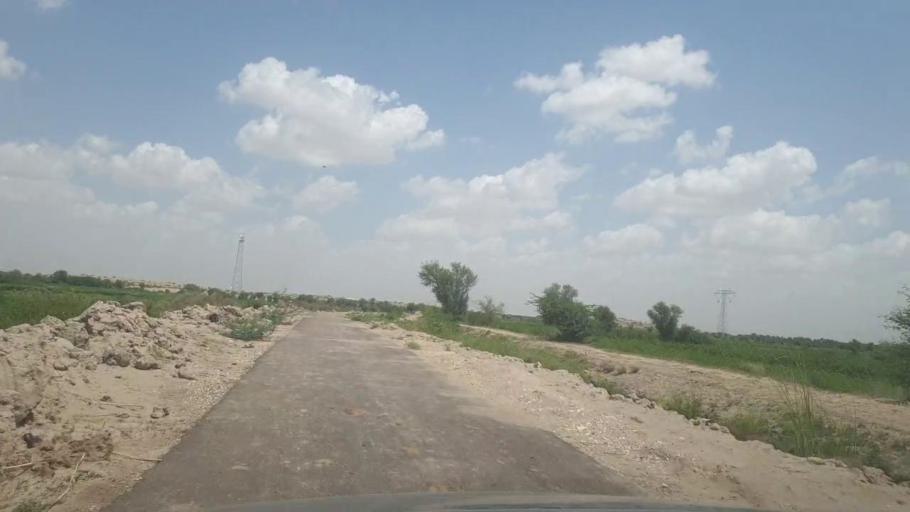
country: PK
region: Sindh
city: Kot Diji
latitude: 27.2336
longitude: 69.0397
